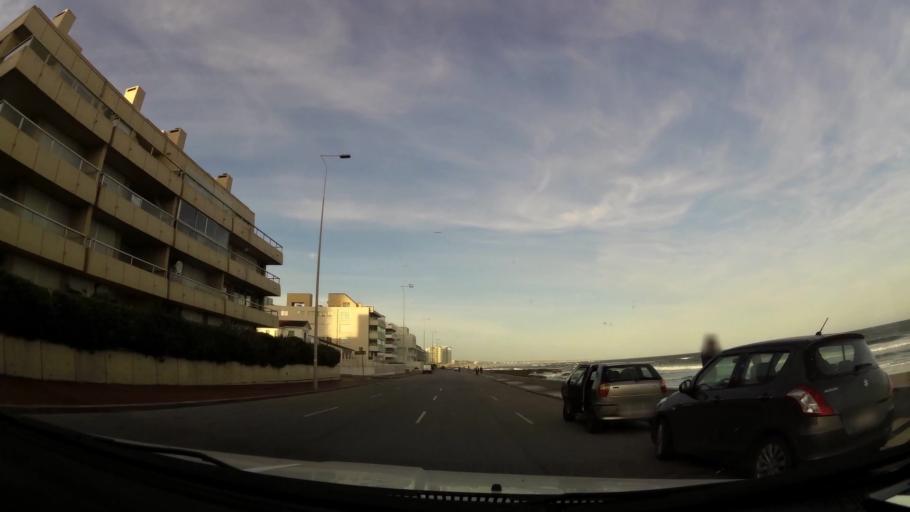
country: UY
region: Maldonado
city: Punta del Este
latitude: -34.9625
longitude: -54.9405
